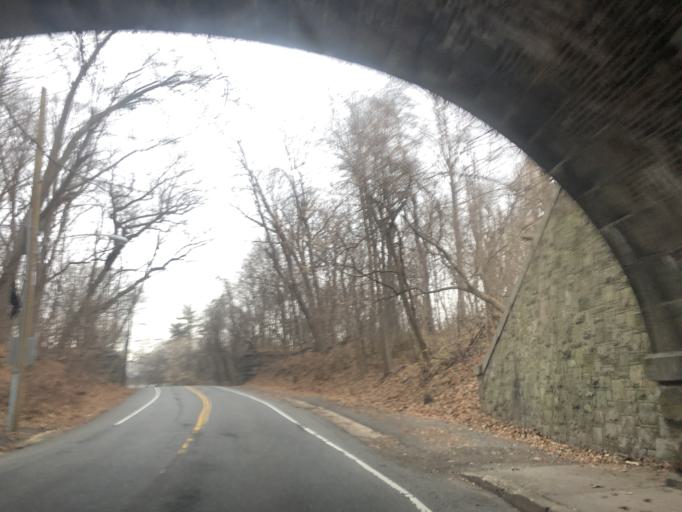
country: US
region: Pennsylvania
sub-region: Montgomery County
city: Bala-Cynwyd
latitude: 39.9973
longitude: -75.2048
